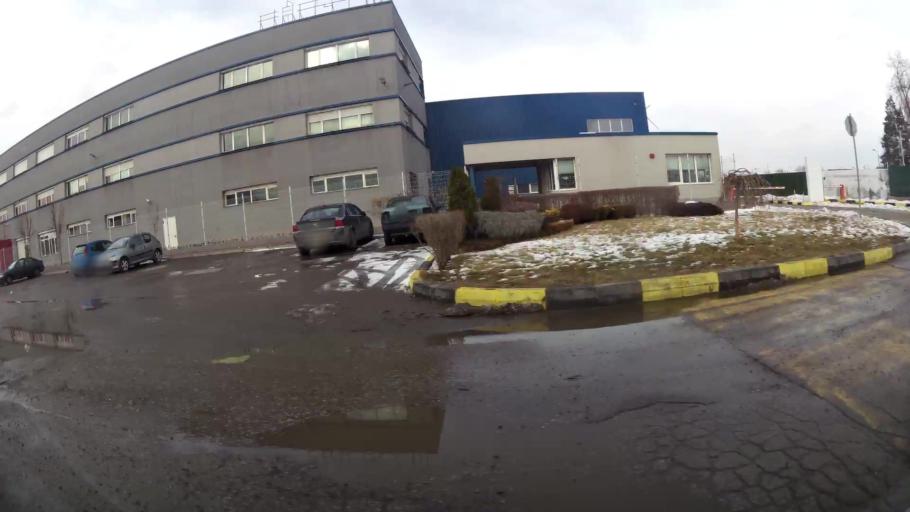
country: BG
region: Sofia-Capital
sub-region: Stolichna Obshtina
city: Sofia
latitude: 42.6936
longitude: 23.3788
